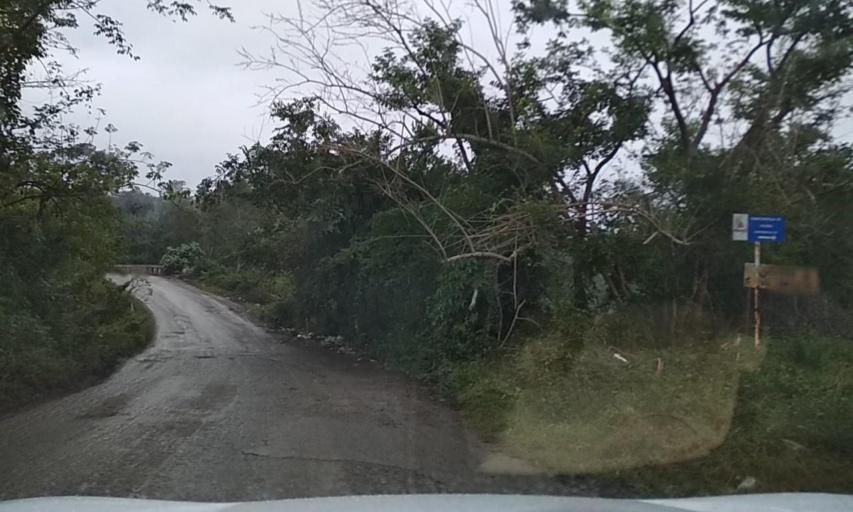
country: MX
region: Veracruz
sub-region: Coatzintla
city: Manuel Maria Contreras
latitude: 20.4612
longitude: -97.4736
